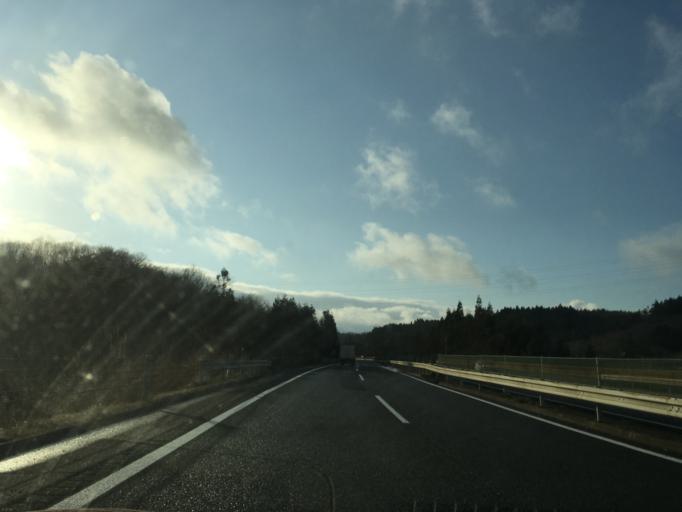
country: JP
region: Miyagi
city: Okawara
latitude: 38.1567
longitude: 140.6881
